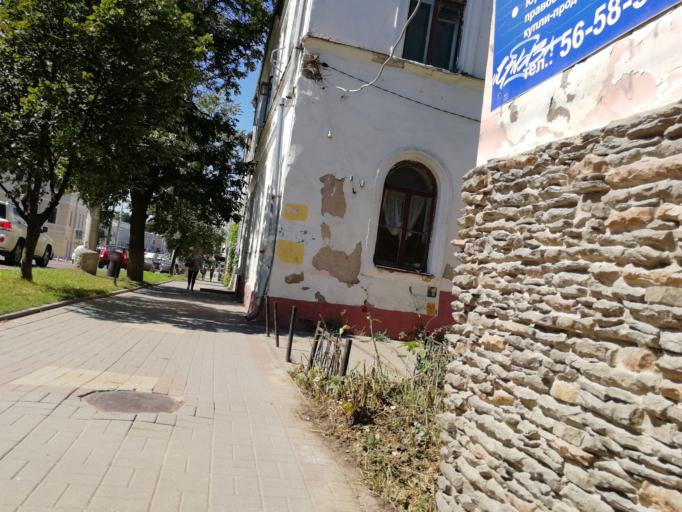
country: RU
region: Kaluga
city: Kaluga
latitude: 54.5058
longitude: 36.2555
